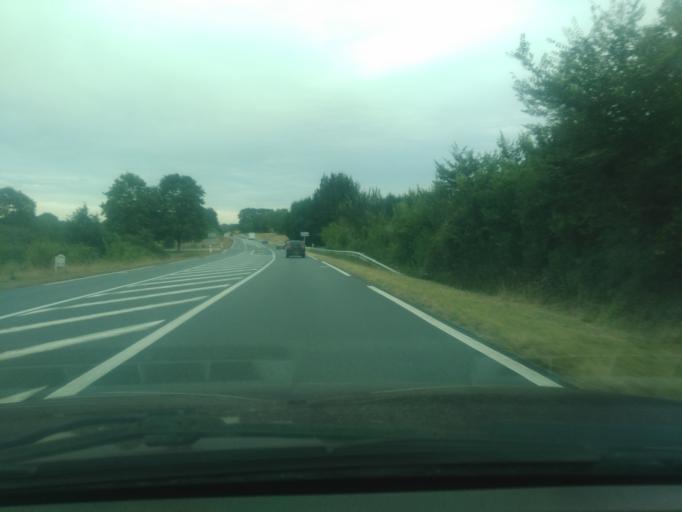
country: FR
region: Centre
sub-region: Departement de l'Indre
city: Saint-Gaultier
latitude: 46.6400
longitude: 1.4076
